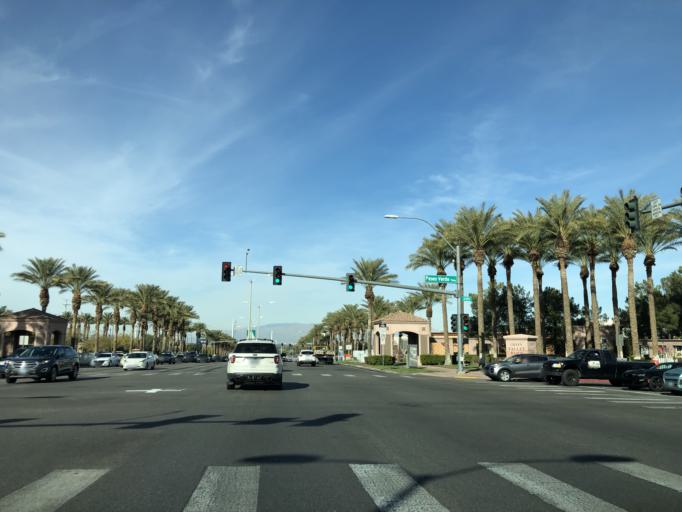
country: US
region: Nevada
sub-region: Clark County
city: Whitney
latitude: 36.0202
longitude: -115.0835
